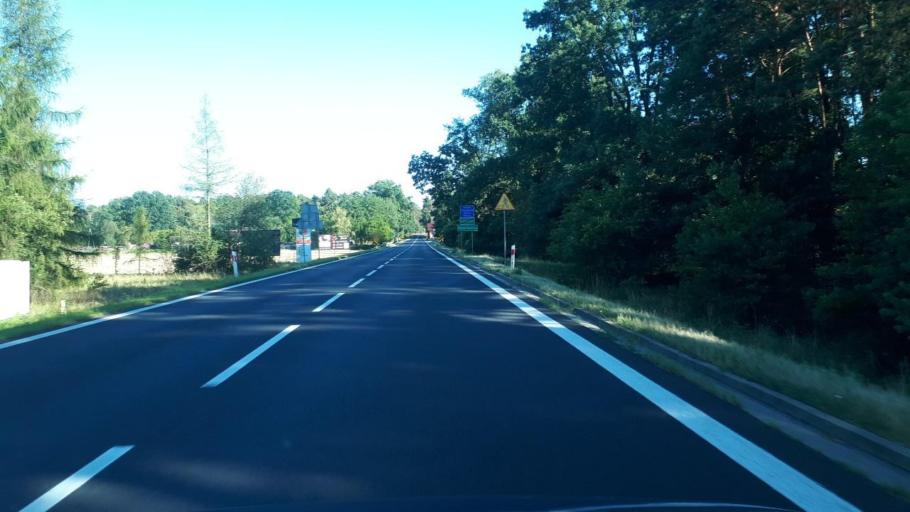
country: PL
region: Silesian Voivodeship
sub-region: Powiat tarnogorski
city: Tworog
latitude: 50.5884
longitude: 18.7030
